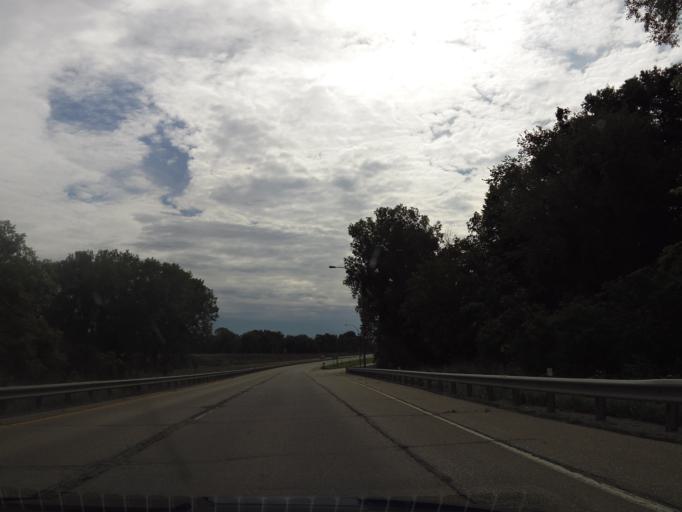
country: US
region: Wisconsin
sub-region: La Crosse County
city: Brice Prairie
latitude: 43.9154
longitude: -91.3664
